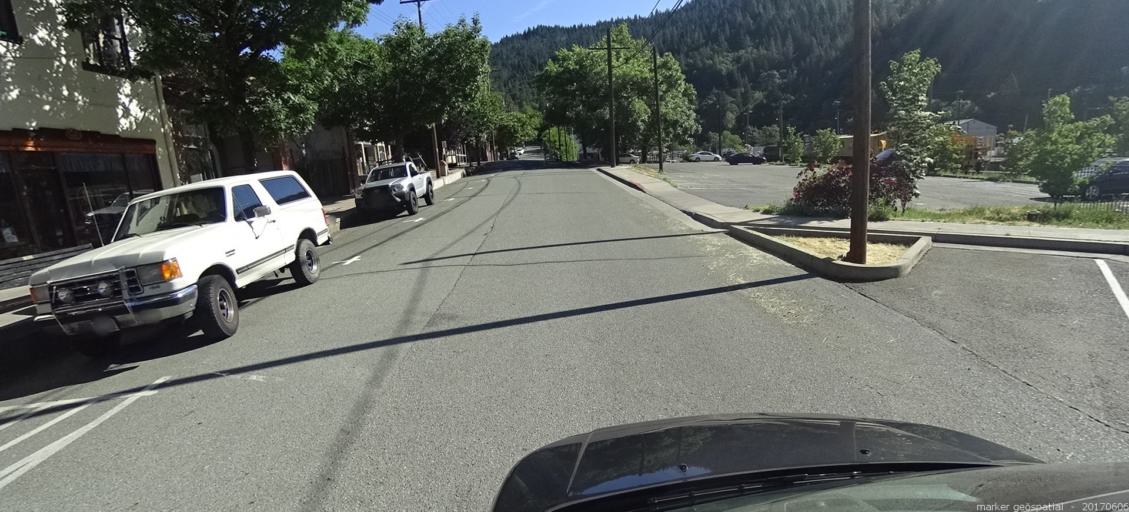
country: US
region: California
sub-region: Siskiyou County
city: Dunsmuir
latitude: 41.2100
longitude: -122.2713
